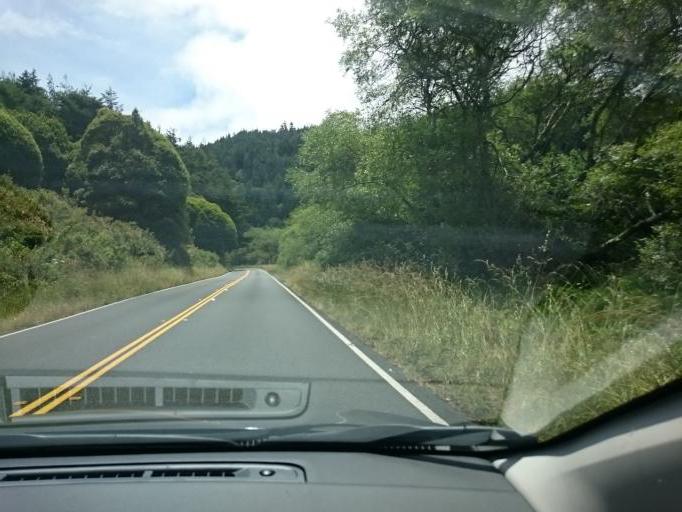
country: US
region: California
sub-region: Mendocino County
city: Fort Bragg
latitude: 39.1908
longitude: -123.7296
